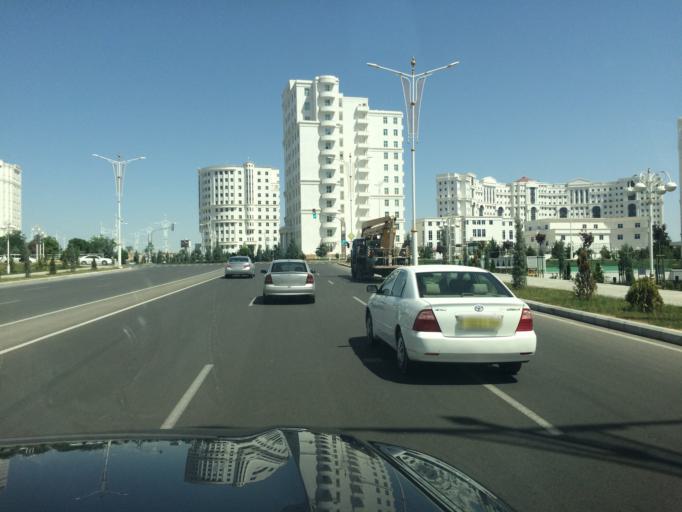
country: TM
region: Ahal
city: Ashgabat
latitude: 37.9190
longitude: 58.3609
